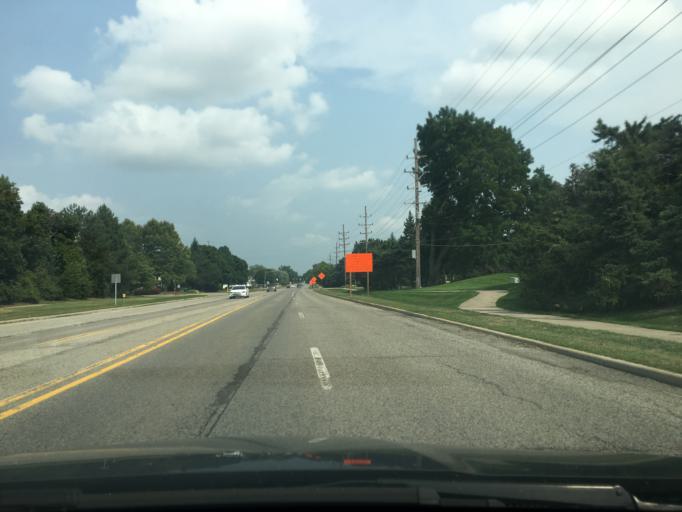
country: US
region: Michigan
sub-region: Oakland County
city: Bloomfield Hills
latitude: 42.6203
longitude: -83.2313
